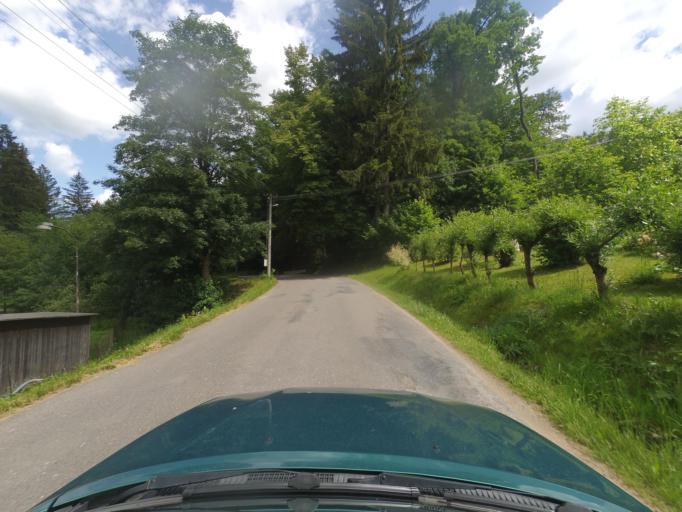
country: CZ
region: Pardubicky
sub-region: Okres Usti nad Orlici
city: Kunvald
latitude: 50.1099
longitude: 16.5465
